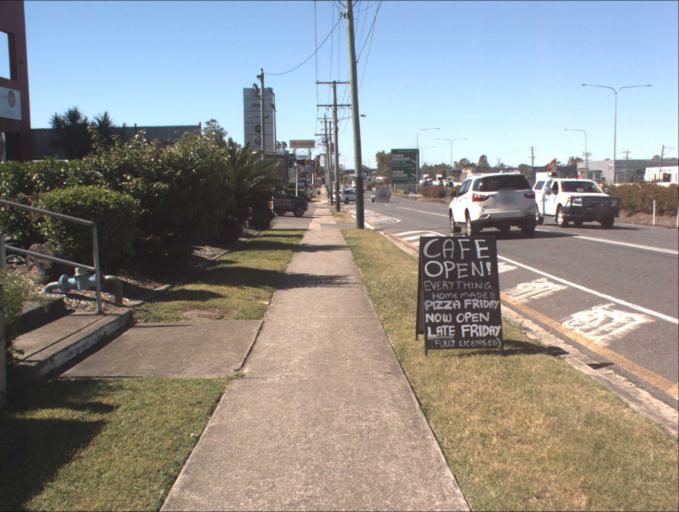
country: AU
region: Queensland
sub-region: Logan
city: Springwood
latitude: -27.6190
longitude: 153.1265
